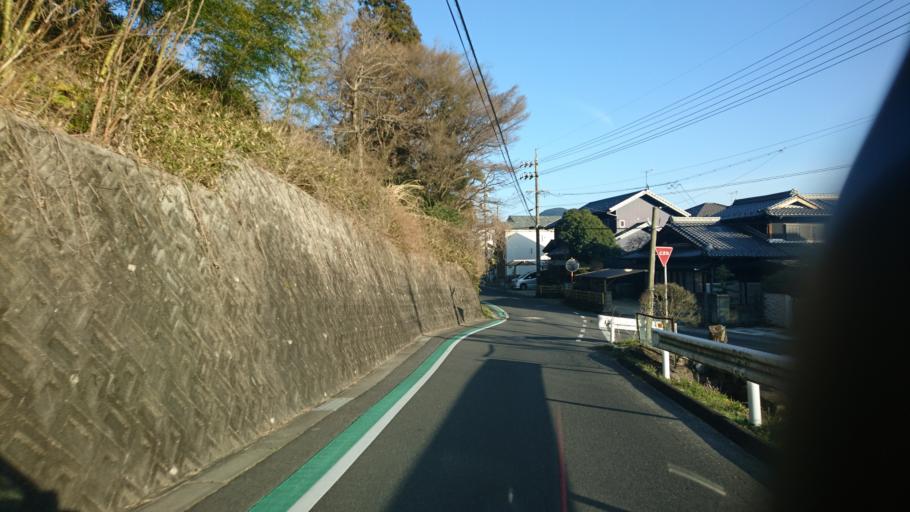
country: JP
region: Gifu
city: Nakatsugawa
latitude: 35.4588
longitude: 137.4102
